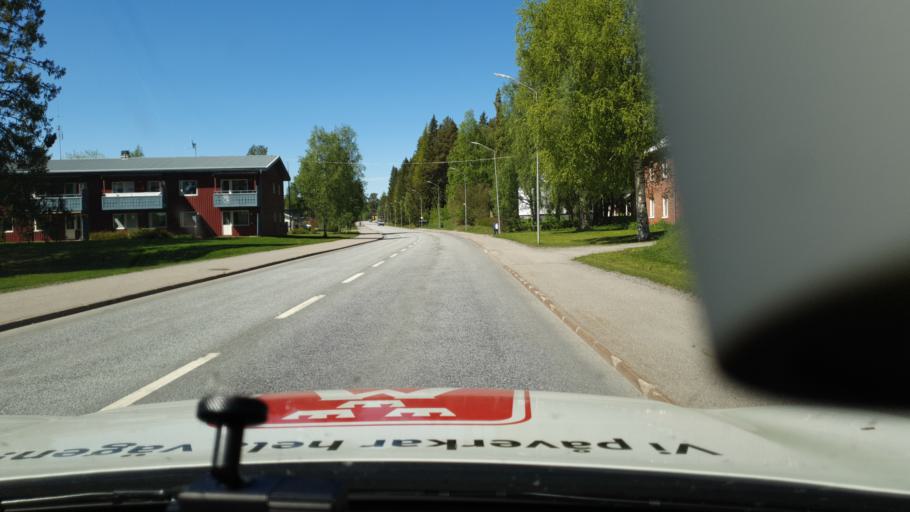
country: SE
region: Vaesterbotten
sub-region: Storumans Kommun
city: Storuman
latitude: 65.0692
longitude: 17.1469
